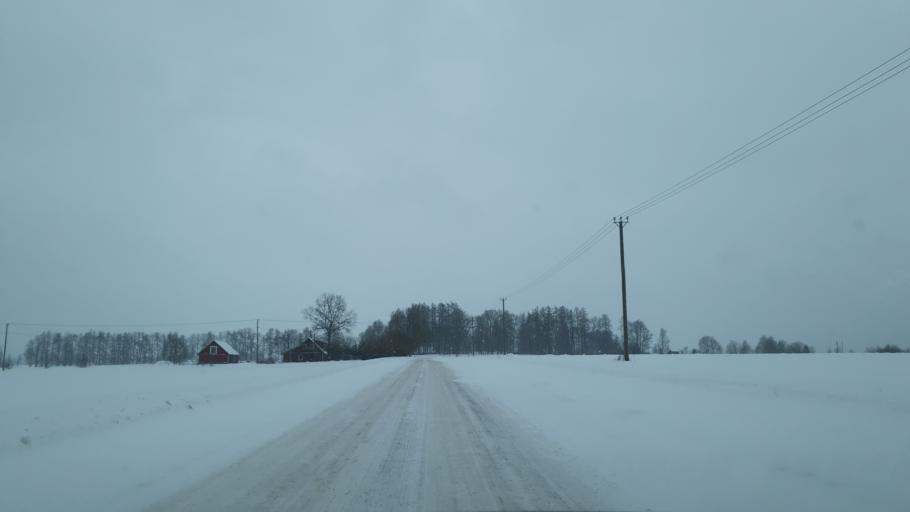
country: EE
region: Tartu
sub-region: Tartu linn
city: Tartu
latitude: 58.5331
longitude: 26.8755
